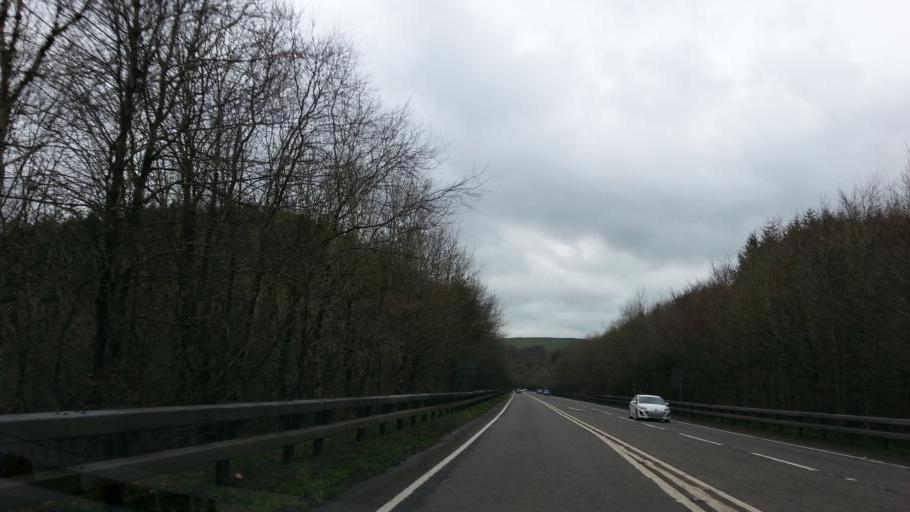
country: GB
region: England
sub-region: Devon
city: South Molton
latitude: 51.0432
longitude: -3.8661
